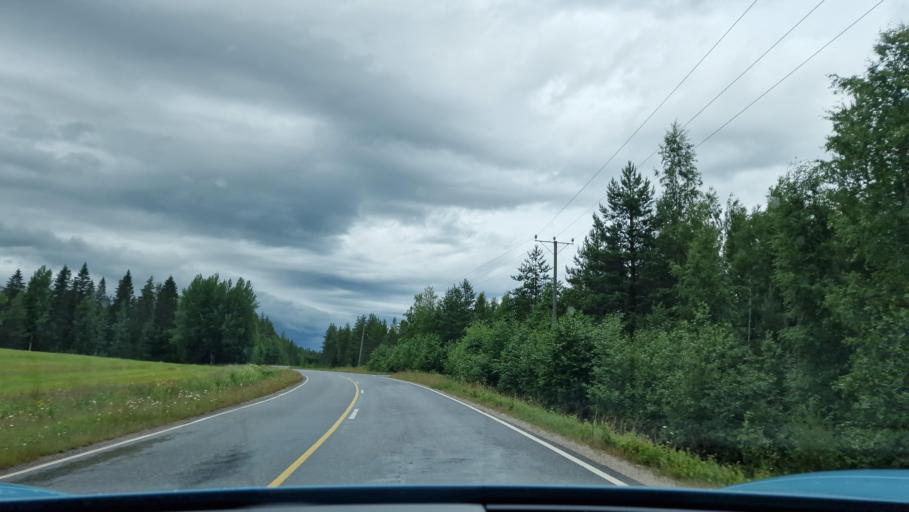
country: FI
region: Southern Ostrobothnia
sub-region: Jaerviseutu
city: Soini
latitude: 62.7285
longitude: 24.4221
